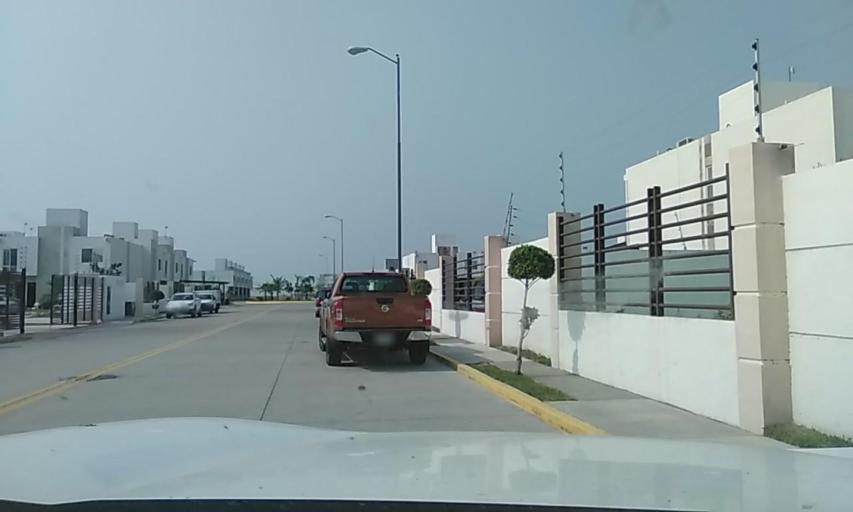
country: MX
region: Veracruz
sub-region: Veracruz
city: Hacienda Sotavento
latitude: 19.1285
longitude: -96.1713
